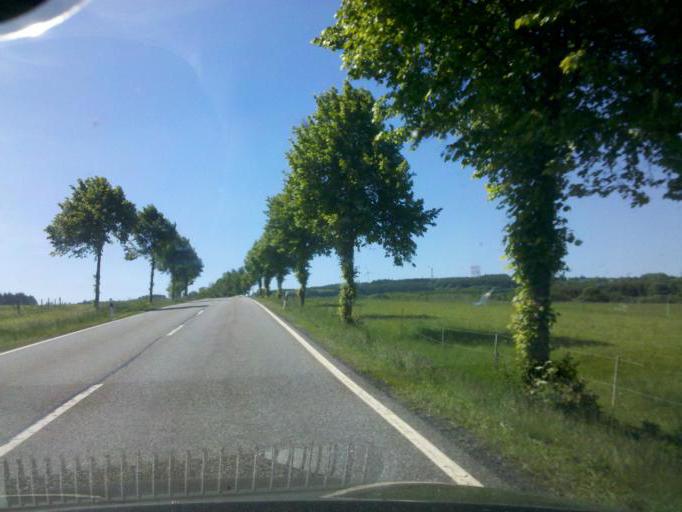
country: DE
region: Rheinland-Pfalz
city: Bretthausen
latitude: 50.6590
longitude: 8.0712
